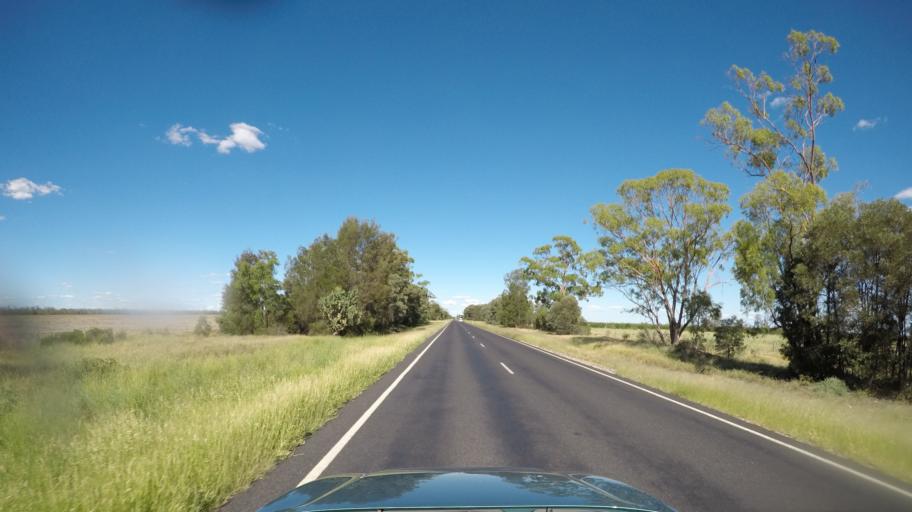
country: AU
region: Queensland
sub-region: Goondiwindi
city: Goondiwindi
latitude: -28.1687
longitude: 150.5160
